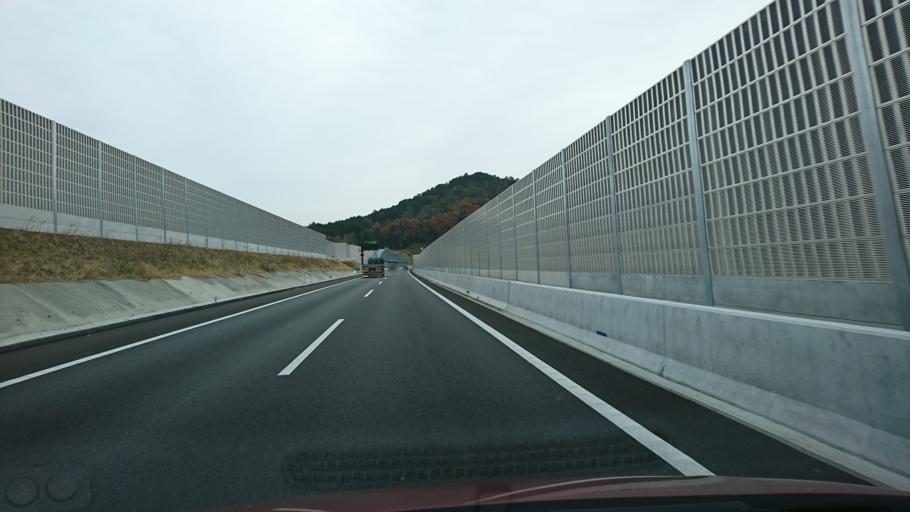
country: JP
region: Hyogo
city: Kawanishi
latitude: 34.8894
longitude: 135.3711
